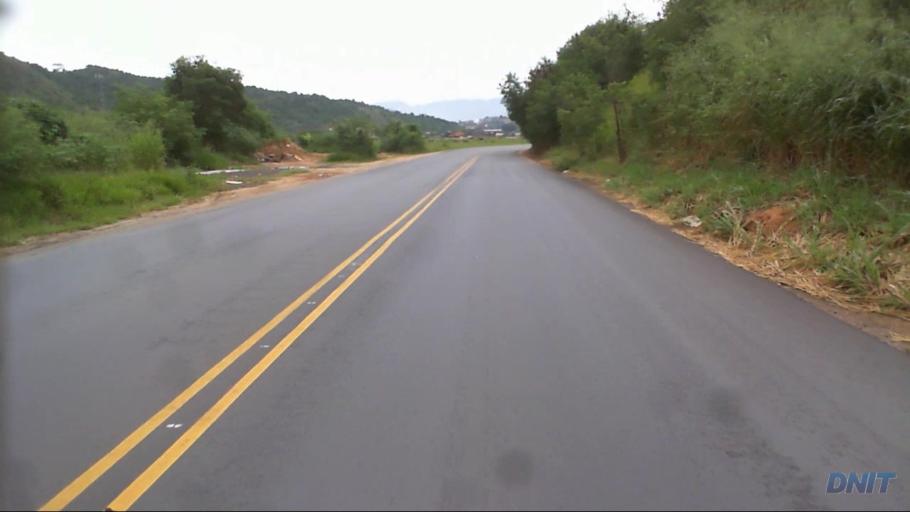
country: BR
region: Minas Gerais
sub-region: Coronel Fabriciano
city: Coronel Fabriciano
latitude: -19.5351
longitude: -42.5948
